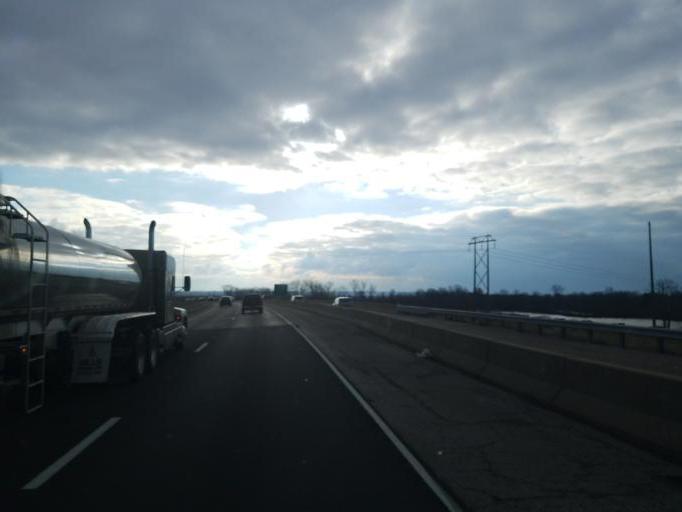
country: US
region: Illinois
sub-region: Madison County
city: Mitchell
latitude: 38.7583
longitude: -90.0909
